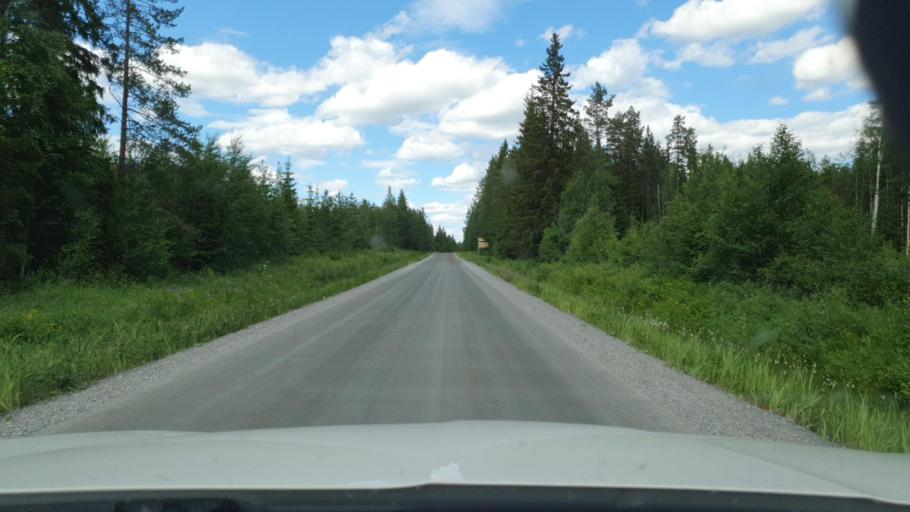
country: SE
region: Vaesterbotten
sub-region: Skelleftea Kommun
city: Forsbacka
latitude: 64.8225
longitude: 20.4965
